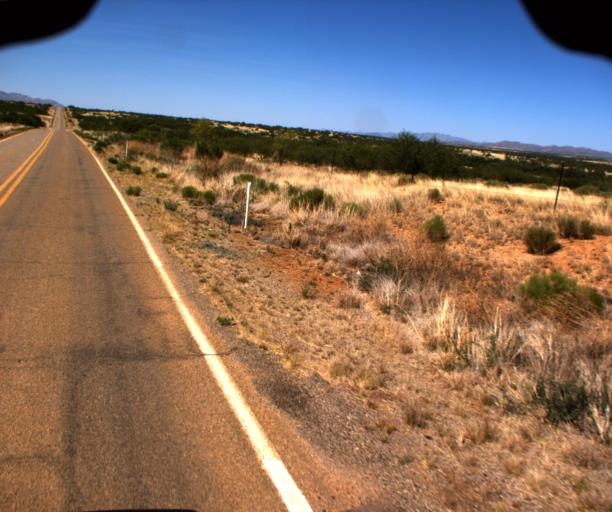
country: US
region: Arizona
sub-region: Santa Cruz County
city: Tubac
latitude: 31.5194
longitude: -111.5422
